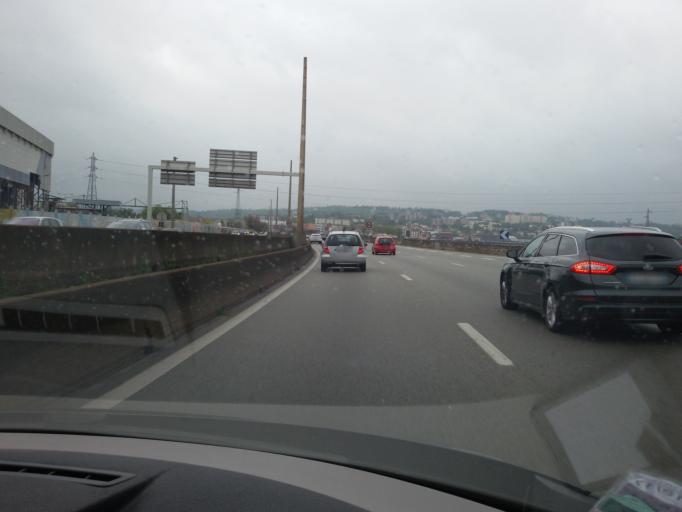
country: FR
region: Rhone-Alpes
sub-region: Departement du Rhone
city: Pierre-Benite
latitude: 45.7096
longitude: 4.8287
